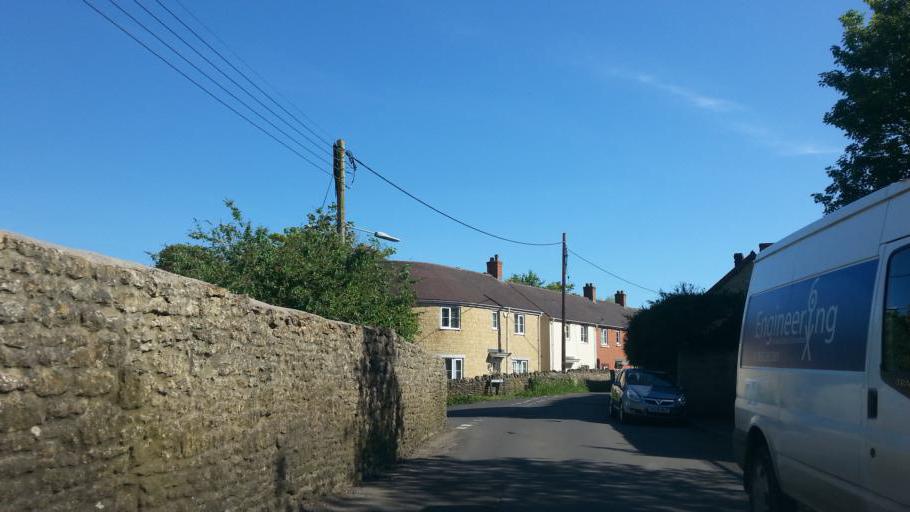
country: GB
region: England
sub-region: Somerset
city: Milborne Port
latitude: 50.9689
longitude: -2.4645
